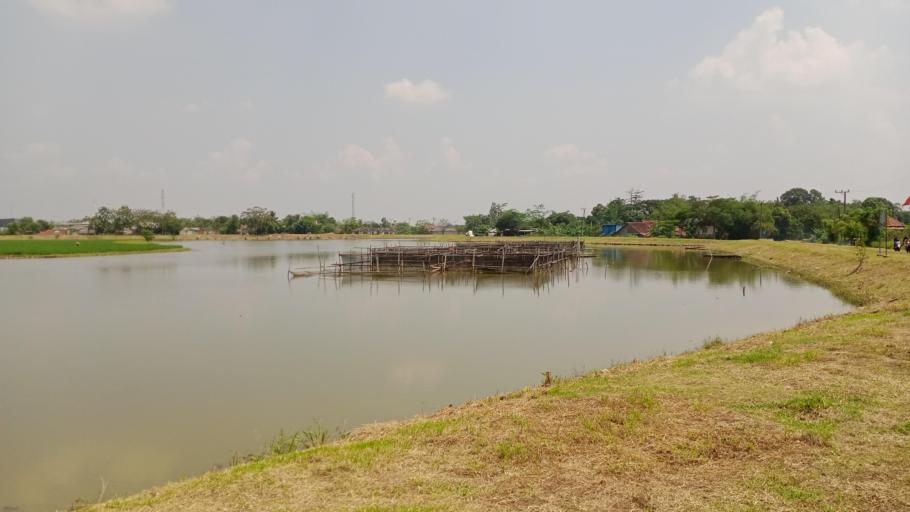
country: ID
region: West Java
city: Cileungsir
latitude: -6.4085
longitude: 107.1028
